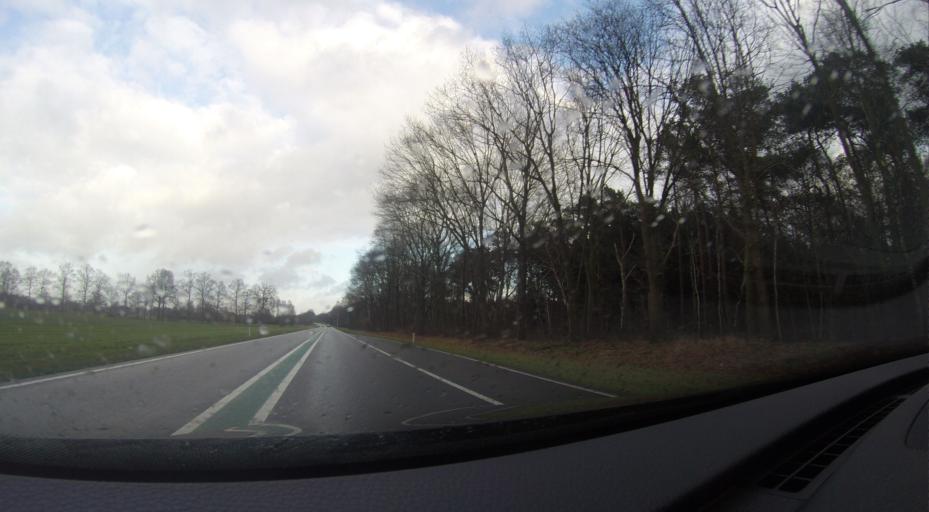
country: NL
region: Gelderland
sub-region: Gemeente Lochem
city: Laren
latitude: 52.2164
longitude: 6.3874
